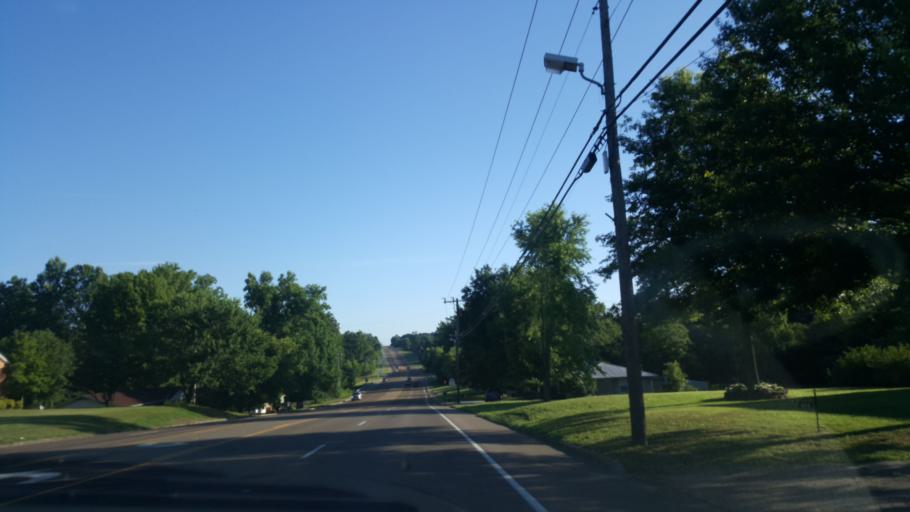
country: US
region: Tennessee
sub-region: Henderson County
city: Lexington
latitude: 35.6654
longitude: -88.3842
